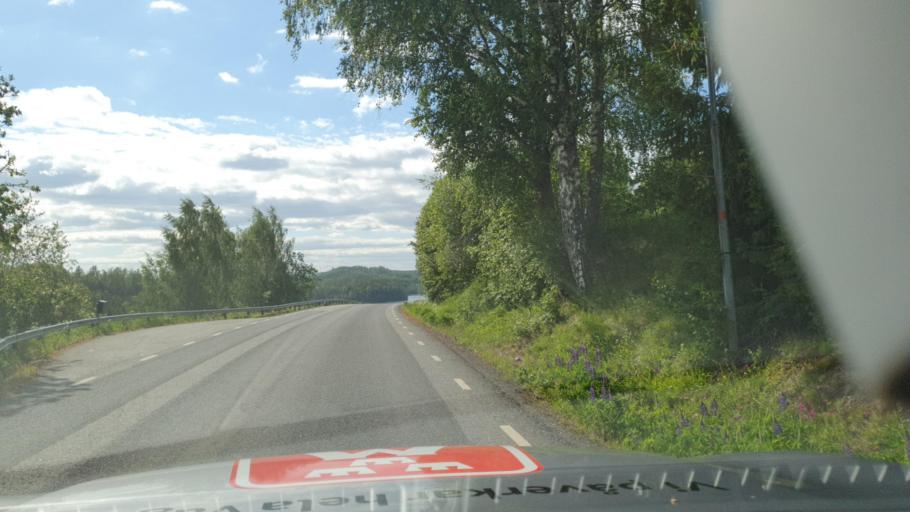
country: SE
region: Vaesternorrland
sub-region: Haernoesands Kommun
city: Haernoesand
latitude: 62.7995
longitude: 18.0824
